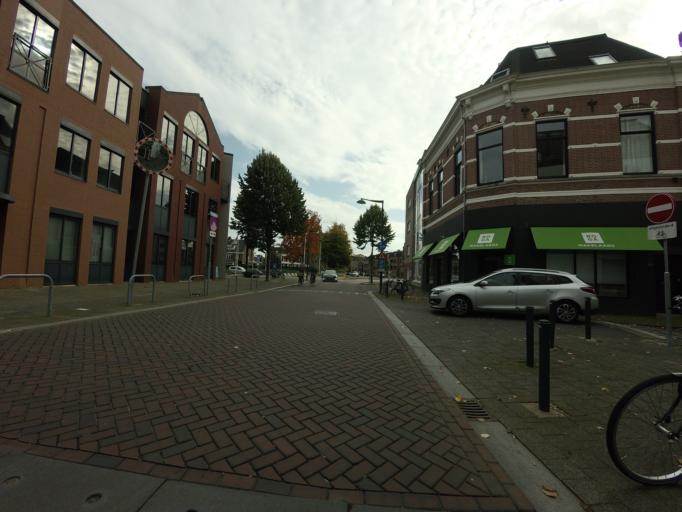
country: NL
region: North Brabant
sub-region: Gemeente Breda
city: Breda
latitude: 51.5742
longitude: 4.7831
